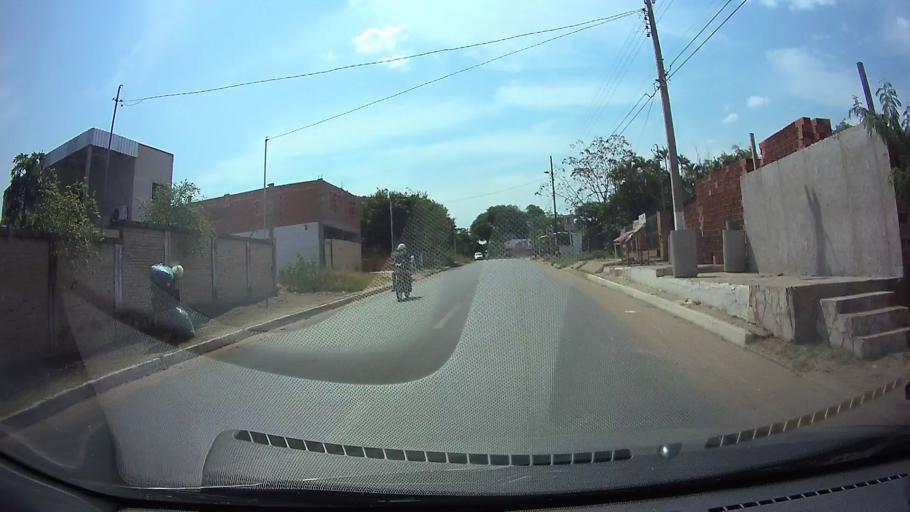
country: PY
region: Central
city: San Lorenzo
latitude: -25.3288
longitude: -57.4975
